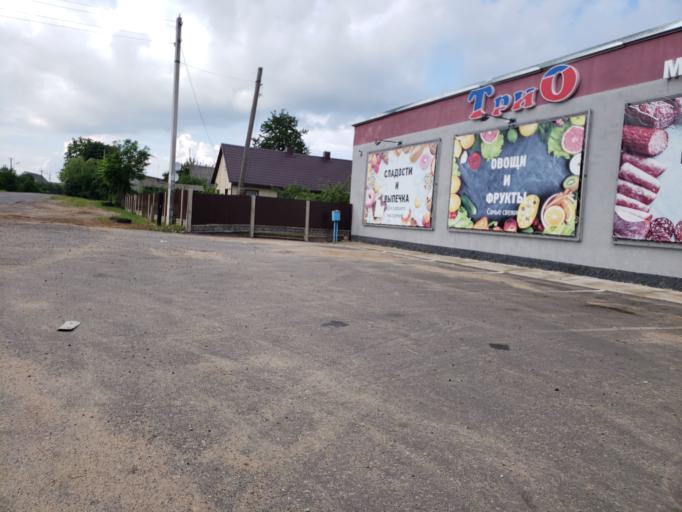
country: BY
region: Minsk
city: Chervyen'
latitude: 53.7350
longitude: 28.3883
